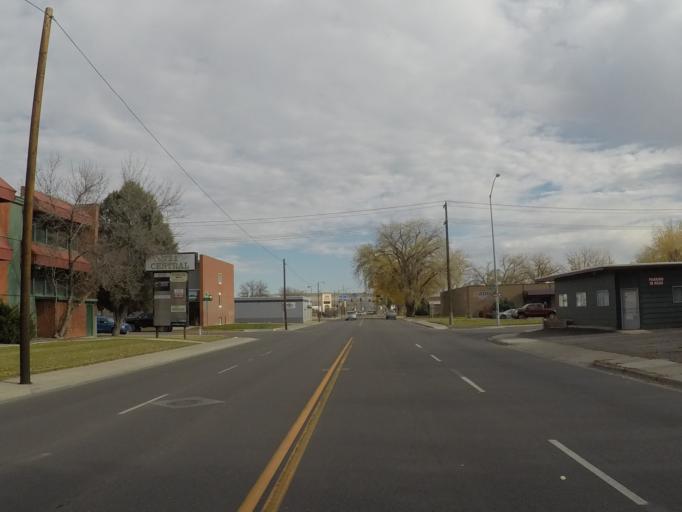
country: US
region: Montana
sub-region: Yellowstone County
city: Billings
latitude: 45.7698
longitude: -108.5337
